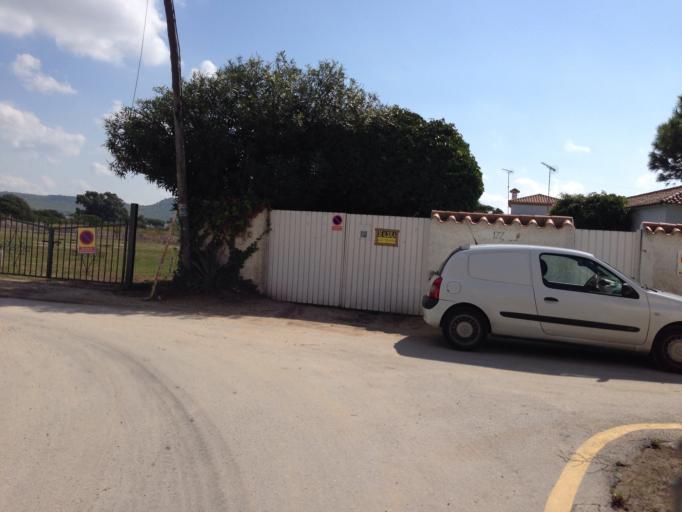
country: ES
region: Andalusia
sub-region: Provincia de Cadiz
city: Vejer de la Frontera
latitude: 36.1981
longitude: -6.0438
